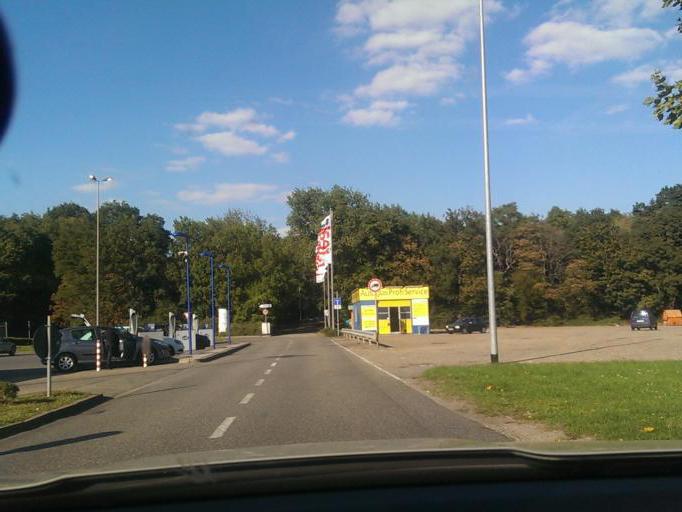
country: DE
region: Baden-Wuerttemberg
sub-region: Karlsruhe Region
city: Karlsruhe
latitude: 49.0048
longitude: 8.4524
